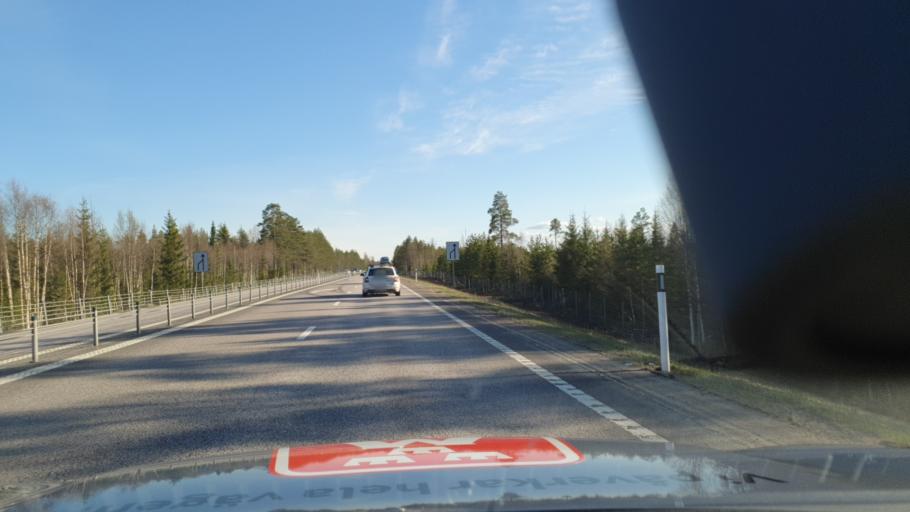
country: SE
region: Norrbotten
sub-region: Pitea Kommun
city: Rosvik
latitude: 65.5002
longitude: 21.7682
